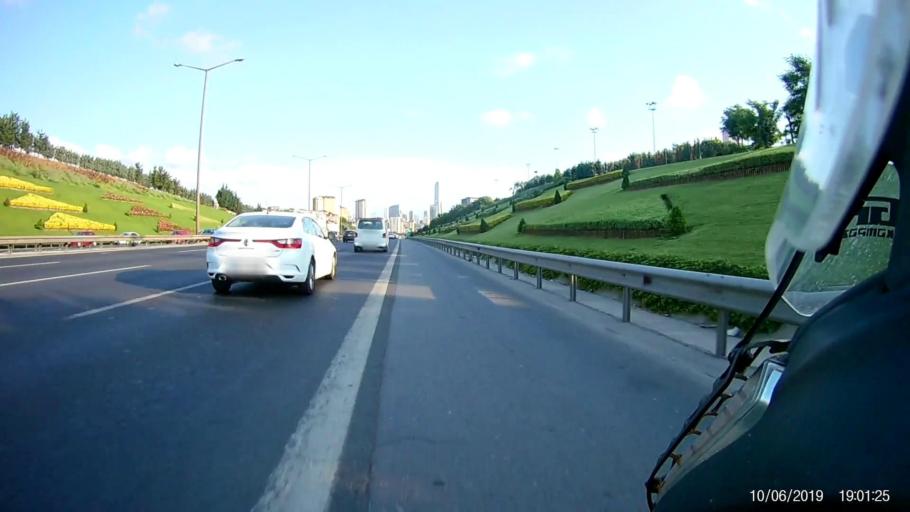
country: TR
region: Istanbul
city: Sancaktepe
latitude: 41.0335
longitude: 29.2561
